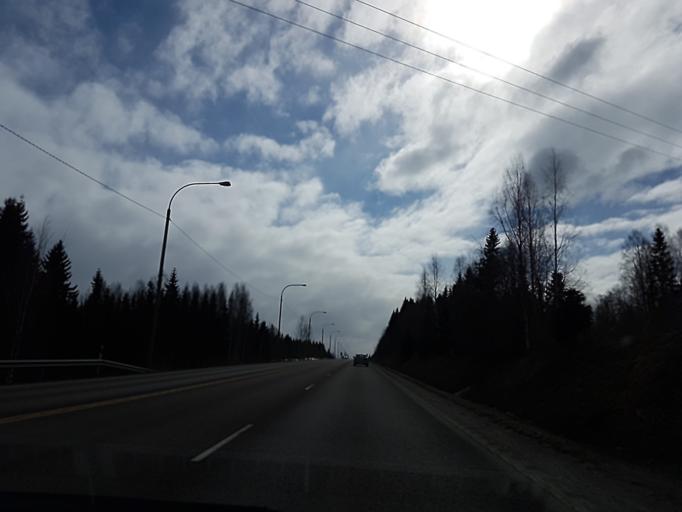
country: FI
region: Northern Savo
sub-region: Varkaus
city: Leppaevirta
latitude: 62.4850
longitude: 27.7693
